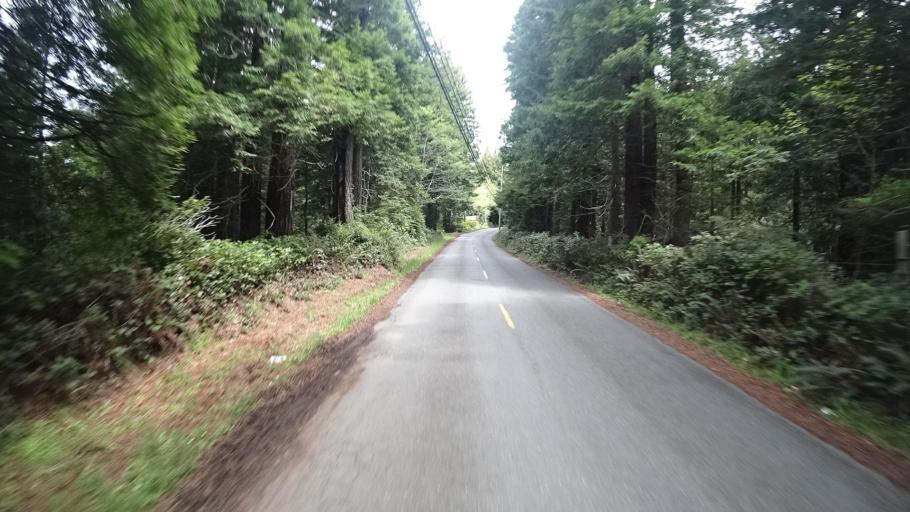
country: US
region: California
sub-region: Humboldt County
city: Bayside
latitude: 40.7986
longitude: -124.0454
